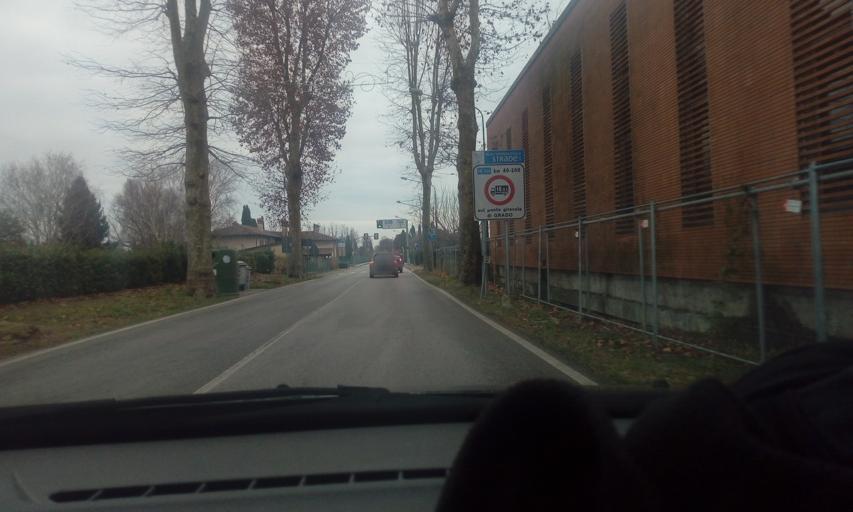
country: IT
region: Friuli Venezia Giulia
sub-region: Provincia di Udine
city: Aquileia
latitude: 45.7752
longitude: 13.3649
